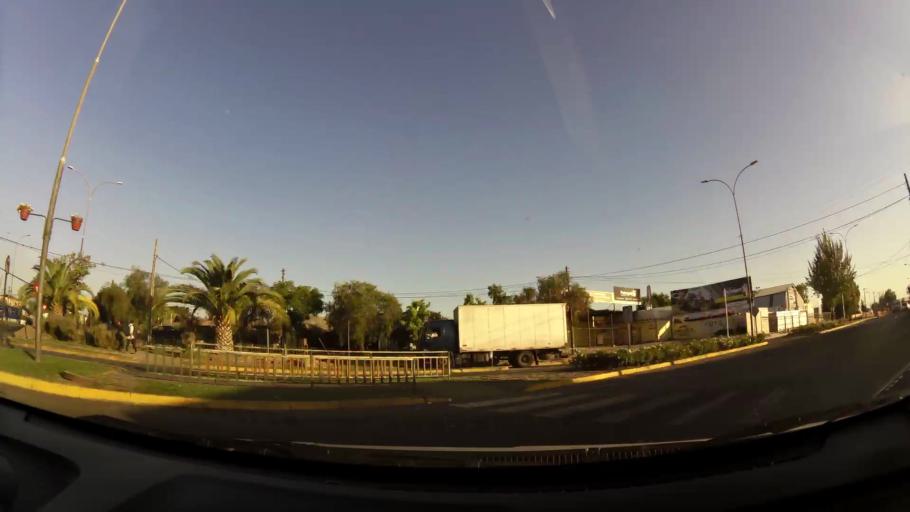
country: CL
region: Maule
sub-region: Provincia de Talca
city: Talca
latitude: -35.4313
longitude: -71.6401
